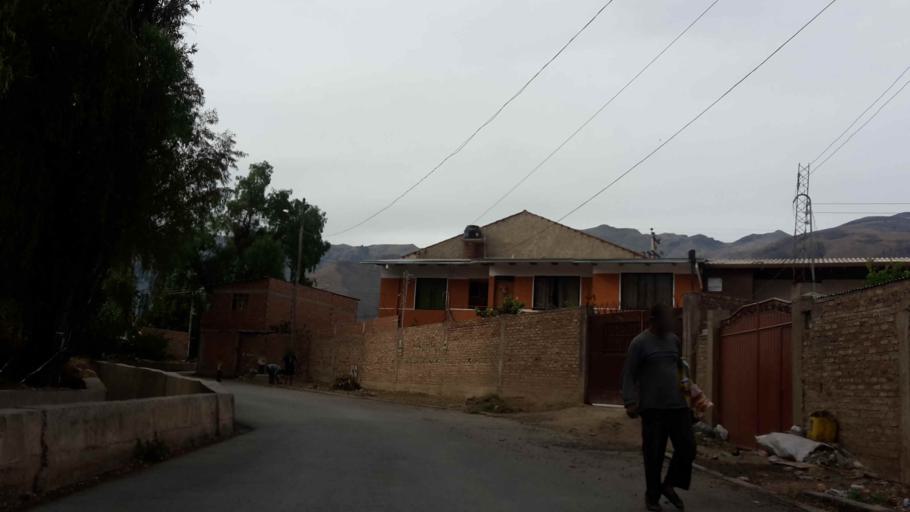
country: BO
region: Cochabamba
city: Cochabamba
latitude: -17.3599
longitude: -66.1911
